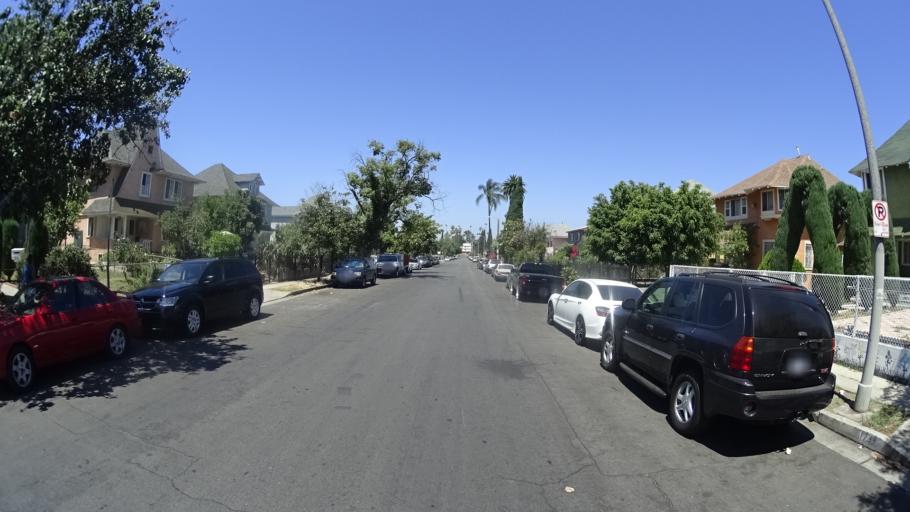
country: US
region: California
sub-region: Los Angeles County
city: Echo Park
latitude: 34.0355
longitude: -118.3011
